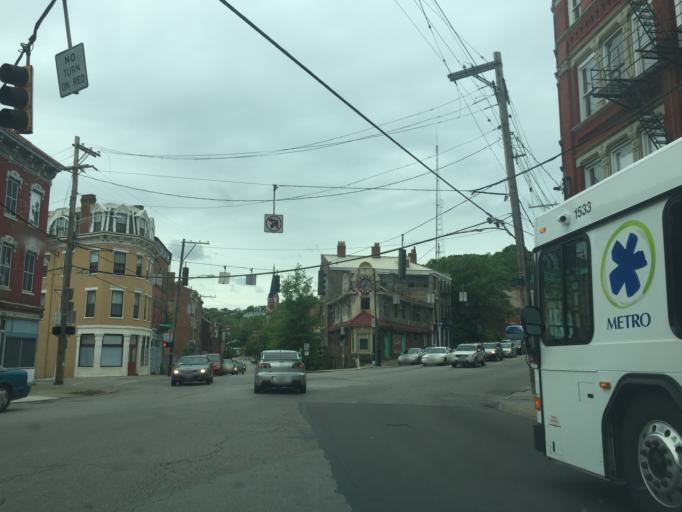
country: US
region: Kentucky
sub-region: Campbell County
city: Newport
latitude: 39.1166
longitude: -84.5167
